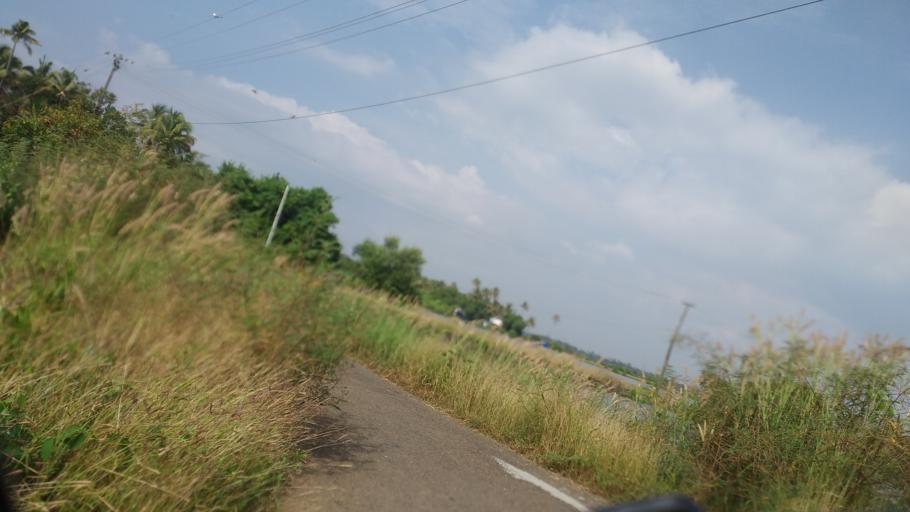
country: IN
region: Kerala
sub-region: Ernakulam
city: Elur
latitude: 10.0861
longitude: 76.2162
